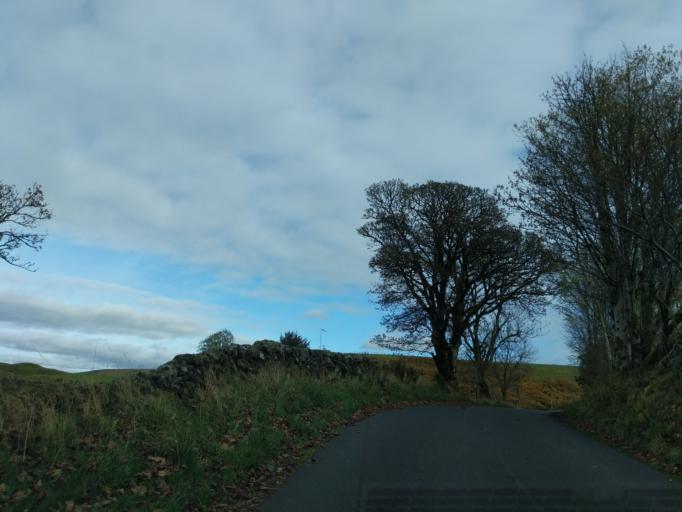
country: GB
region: Scotland
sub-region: Dumfries and Galloway
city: Castle Douglas
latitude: 55.1125
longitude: -4.1050
